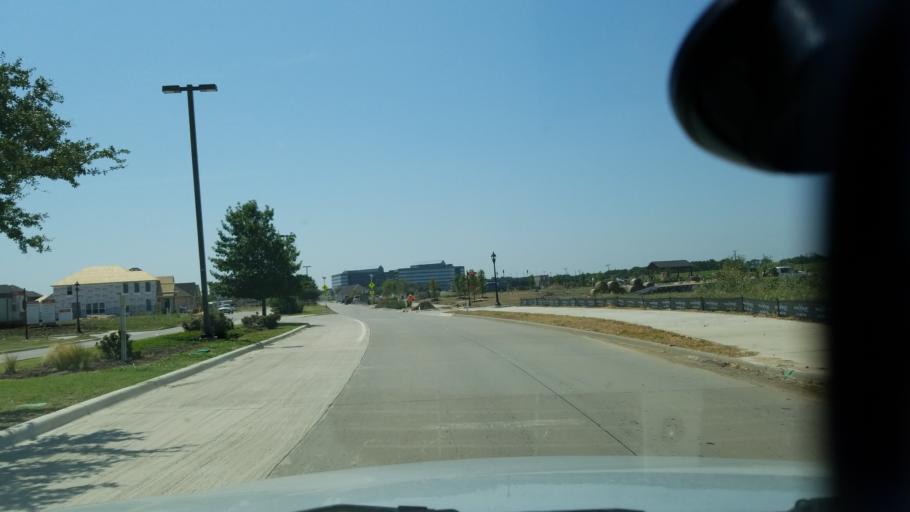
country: US
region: Texas
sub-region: Dallas County
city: Farmers Branch
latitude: 32.9170
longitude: -96.9314
